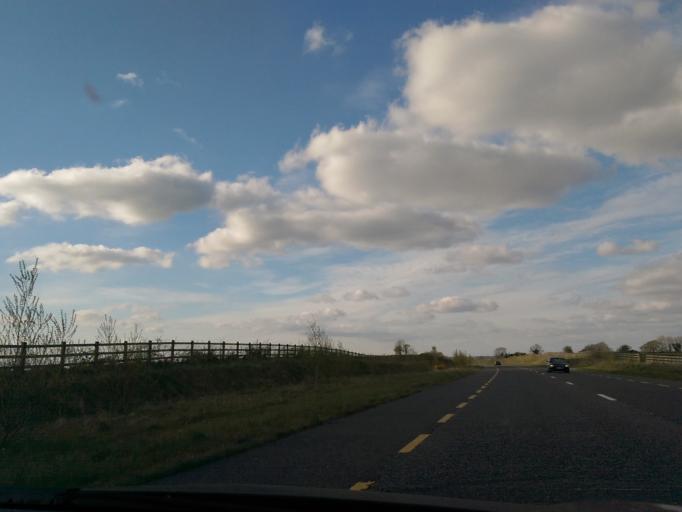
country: IE
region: Connaught
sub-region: County Galway
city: Loughrea
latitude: 53.2452
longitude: -8.5938
